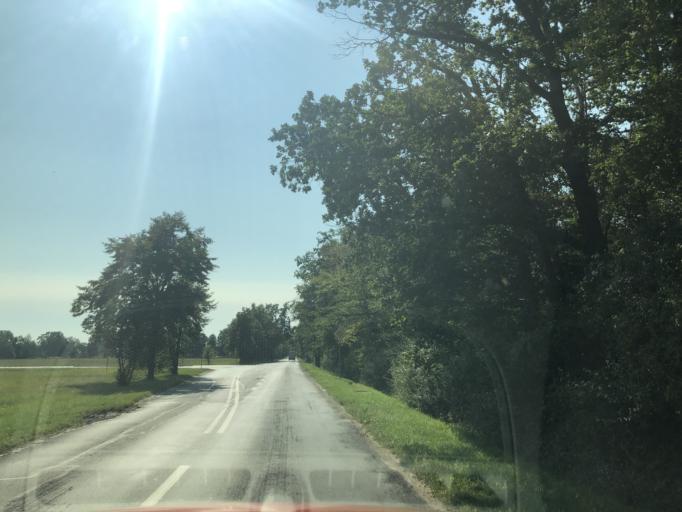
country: PL
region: Lower Silesian Voivodeship
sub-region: Powiat wroclawski
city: Smolec
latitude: 51.1701
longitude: 16.9154
